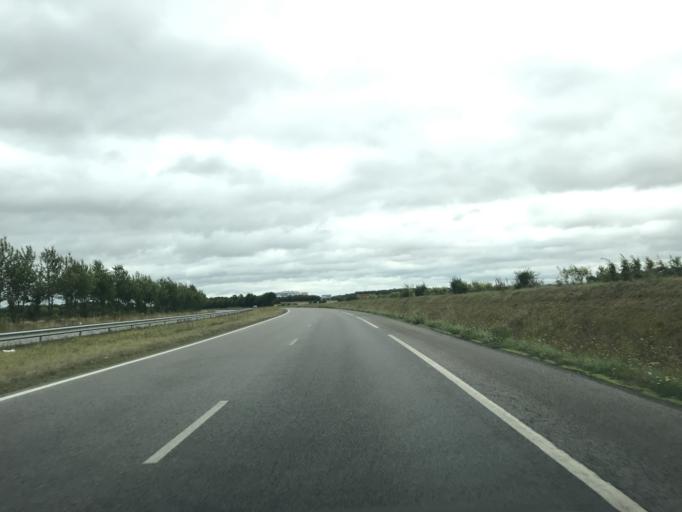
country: FR
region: Haute-Normandie
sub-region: Departement de l'Eure
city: Evreux
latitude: 48.9969
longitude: 1.1711
